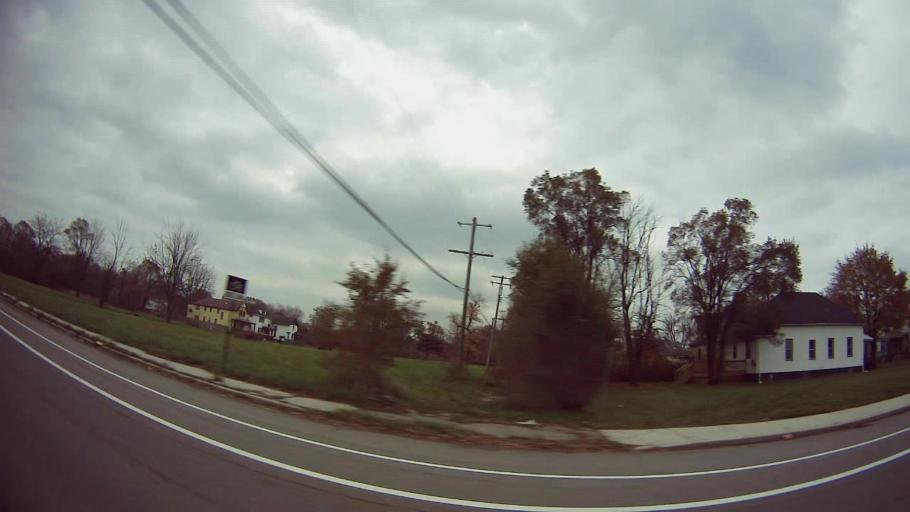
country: US
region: Michigan
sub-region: Wayne County
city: Hamtramck
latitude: 42.3729
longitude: -83.0139
